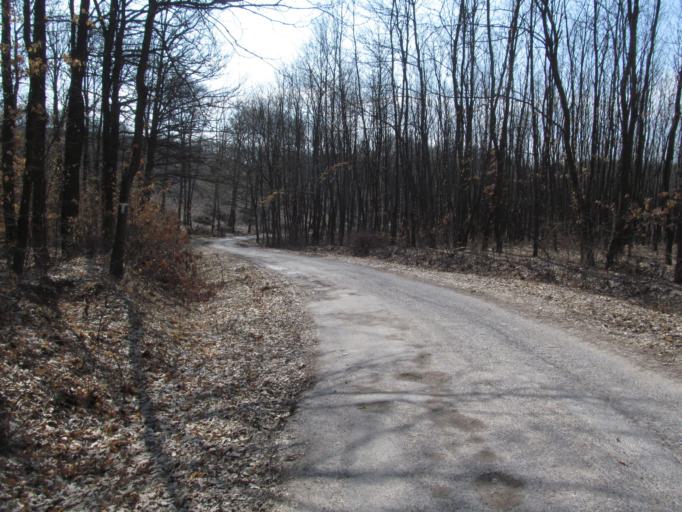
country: HU
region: Borsod-Abauj-Zemplen
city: Putnok
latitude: 48.3474
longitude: 20.4384
